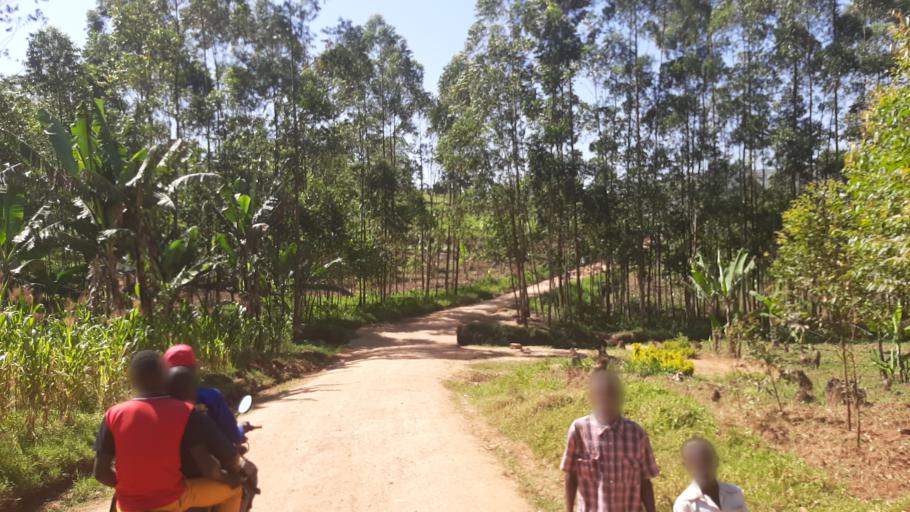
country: UG
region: Eastern Region
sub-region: Manafwa District
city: Manafwa
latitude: 0.9126
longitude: 34.3300
